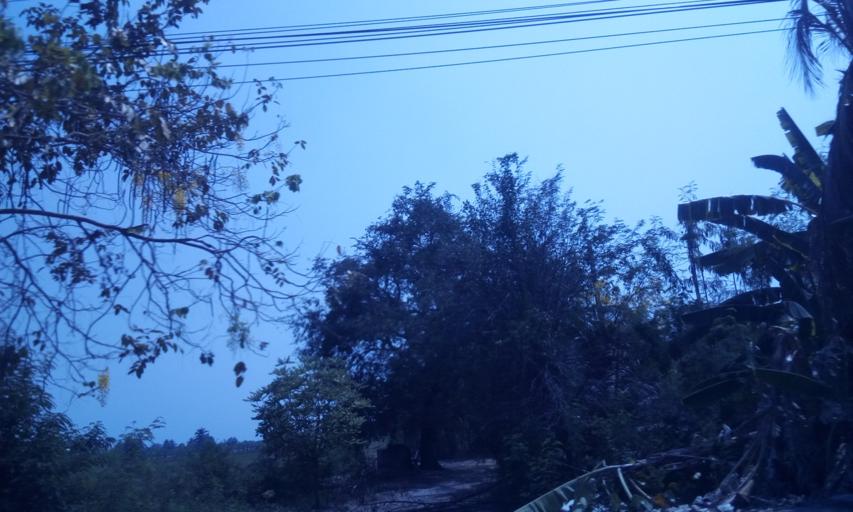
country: TH
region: Nonthaburi
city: Bang Yai
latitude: 13.9090
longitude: 100.3490
